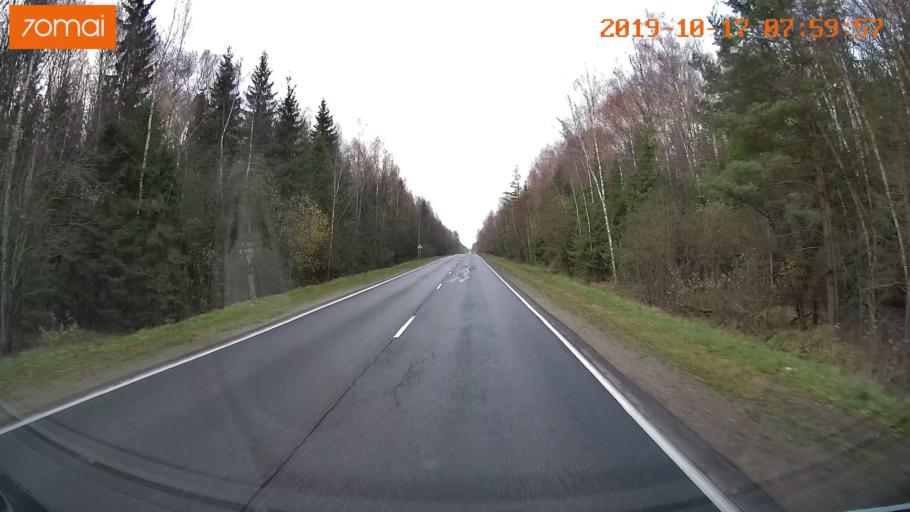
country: RU
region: Vladimir
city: Bavleny
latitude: 56.3883
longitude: 39.5280
